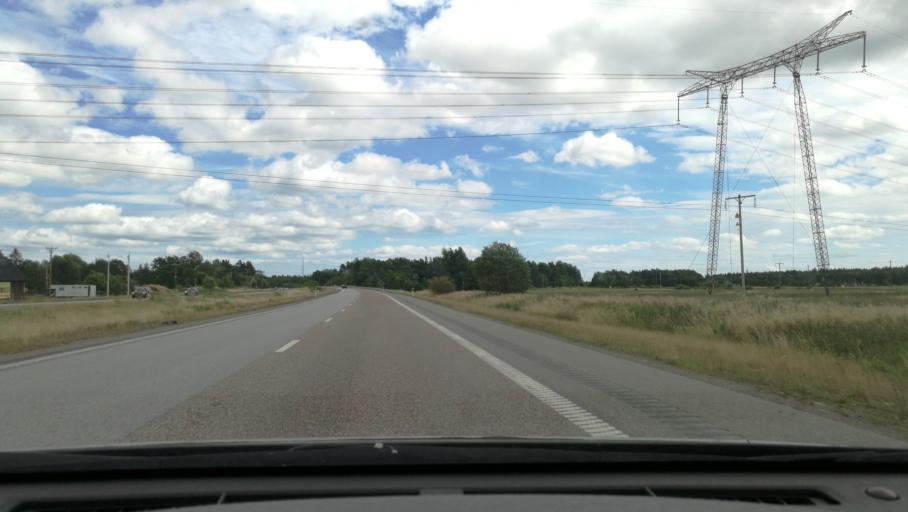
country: SE
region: Uppsala
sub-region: Habo Kommun
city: Balsta
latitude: 59.5953
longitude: 17.4573
